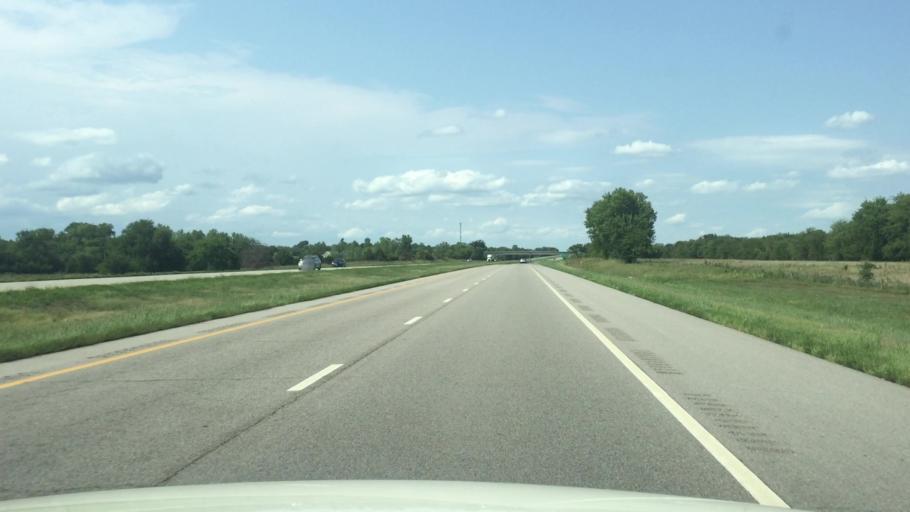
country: US
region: Kansas
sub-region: Linn County
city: La Cygne
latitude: 38.4549
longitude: -94.6861
